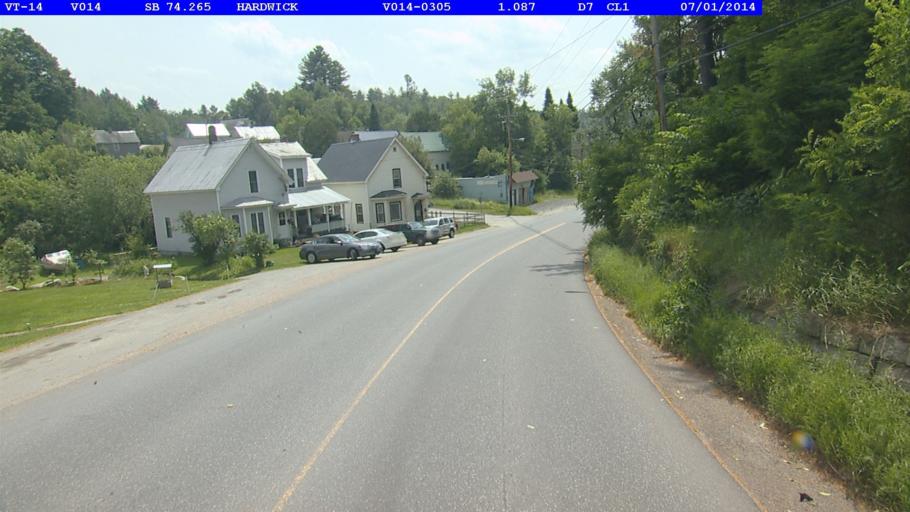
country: US
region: Vermont
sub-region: Caledonia County
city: Hardwick
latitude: 44.4993
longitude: -72.3715
